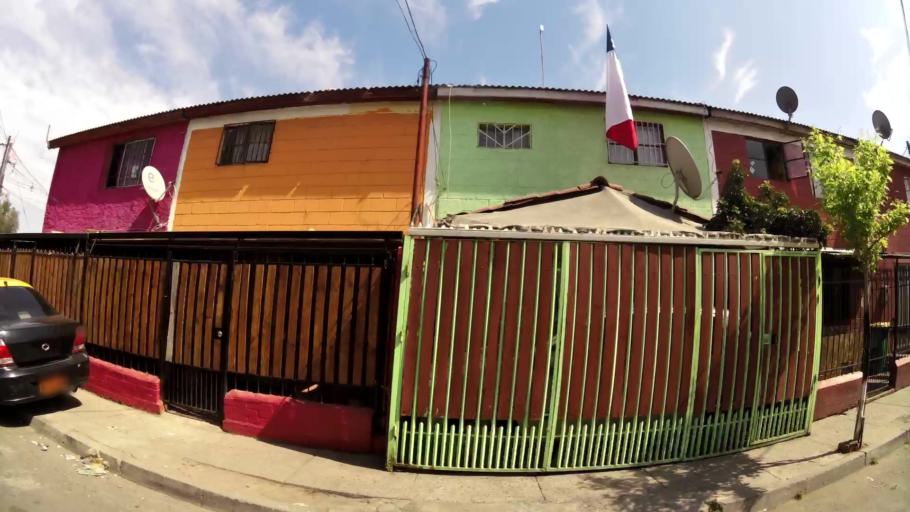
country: CL
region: Santiago Metropolitan
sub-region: Provincia de Santiago
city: La Pintana
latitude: -33.5609
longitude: -70.6366
